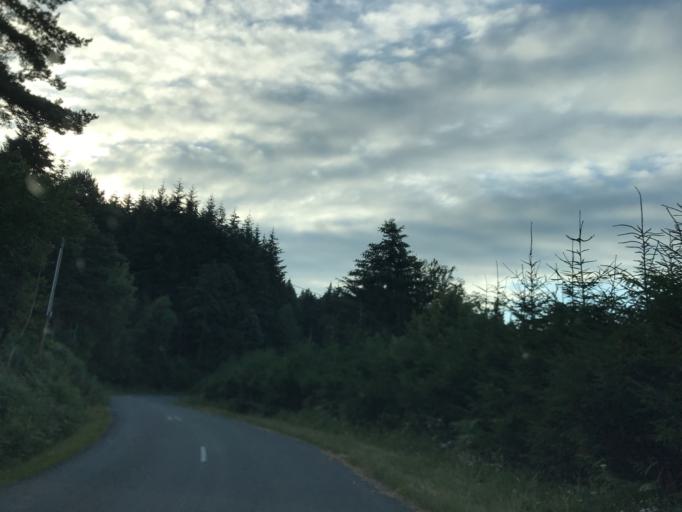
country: FR
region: Rhone-Alpes
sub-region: Departement de la Loire
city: Noiretable
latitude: 45.7482
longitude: 3.8425
